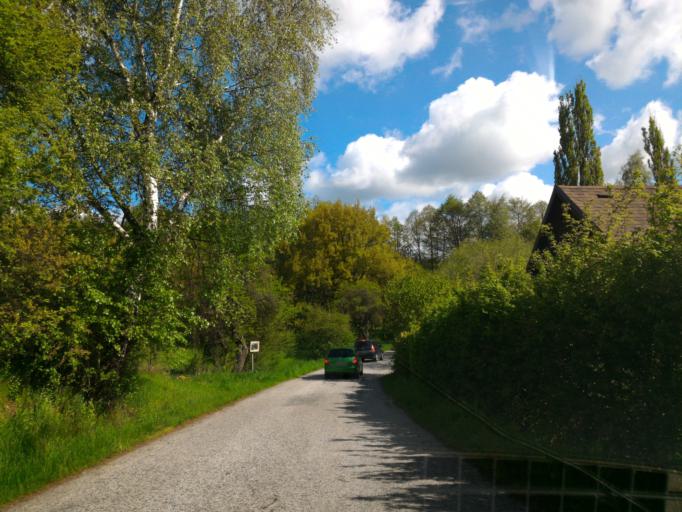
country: CZ
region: Vysocina
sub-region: Okres Havlickuv Brod
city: Svetla nad Sazavou
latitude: 49.6261
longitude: 15.3380
